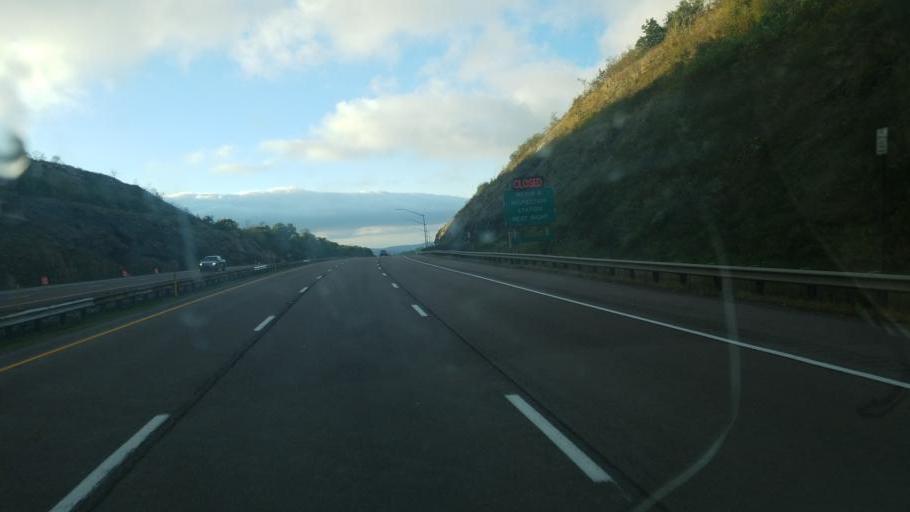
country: US
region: Maryland
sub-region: Allegany County
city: Frostburg
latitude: 39.6744
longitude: -78.9634
